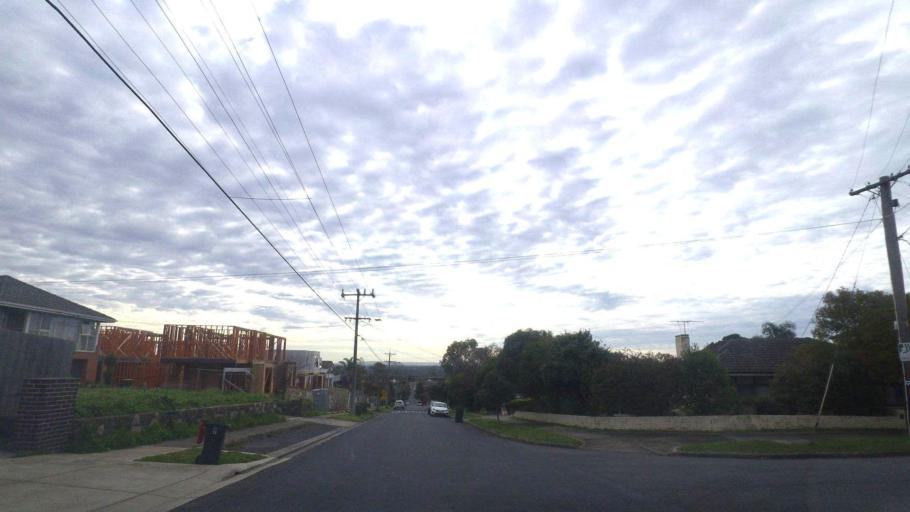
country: AU
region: Victoria
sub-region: Manningham
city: Templestowe Lower
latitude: -37.7719
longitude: 145.1075
